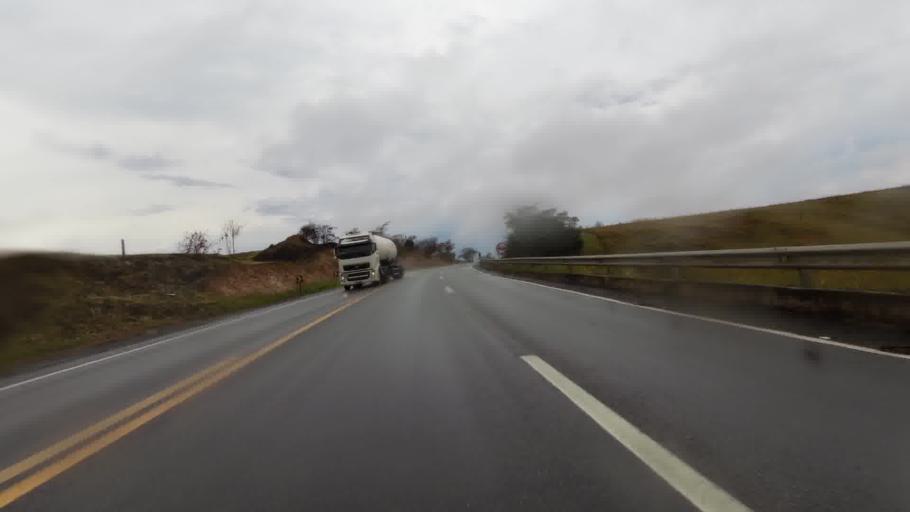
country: BR
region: Rio de Janeiro
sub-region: Campos Dos Goytacazes
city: Campos
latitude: -21.5123
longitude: -41.3345
